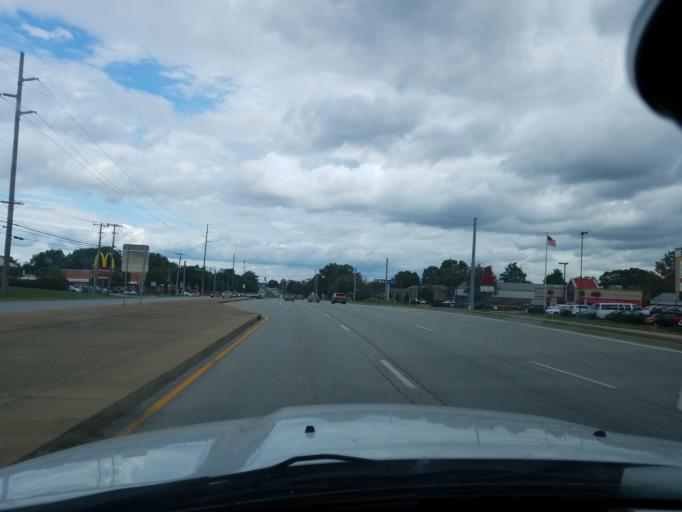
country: US
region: Kentucky
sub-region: Jefferson County
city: Hurstbourne Acres
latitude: 38.2272
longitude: -85.5775
